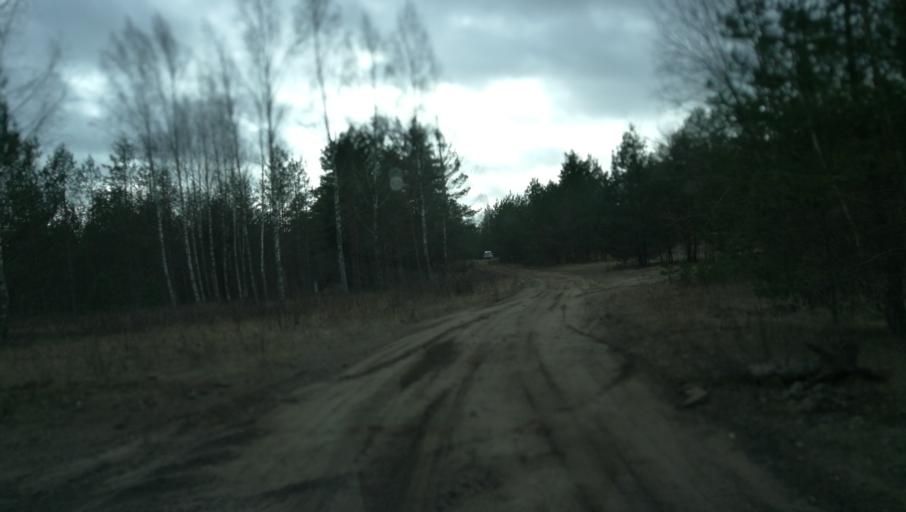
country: LV
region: Adazi
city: Adazi
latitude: 57.0591
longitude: 24.2589
